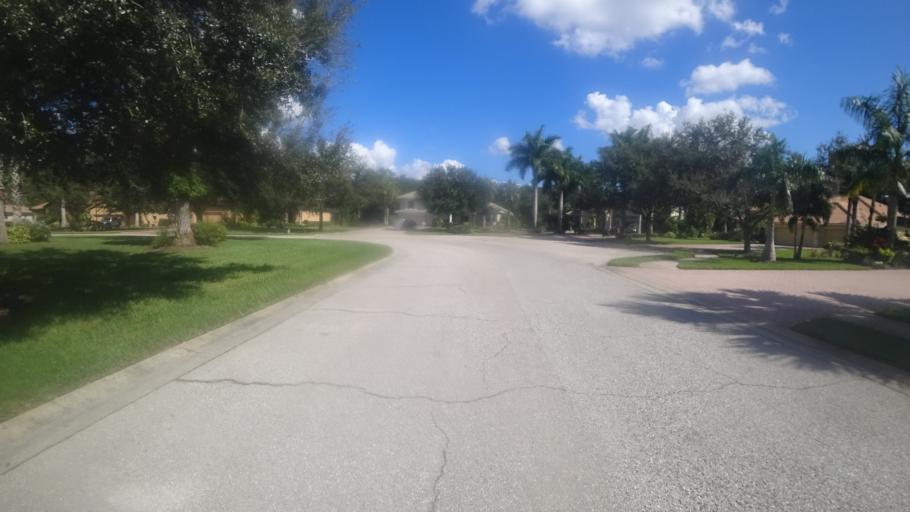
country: US
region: Florida
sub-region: Manatee County
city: Ellenton
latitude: 27.4994
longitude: -82.3939
